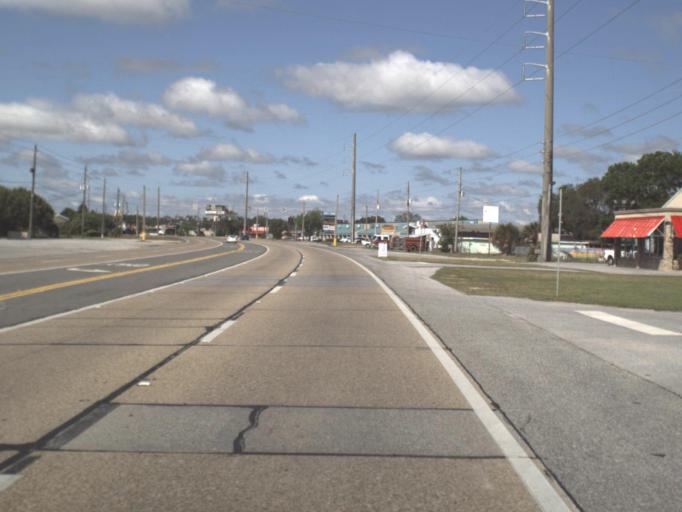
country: US
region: Florida
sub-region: Escambia County
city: West Pensacola
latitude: 30.4093
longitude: -87.2696
